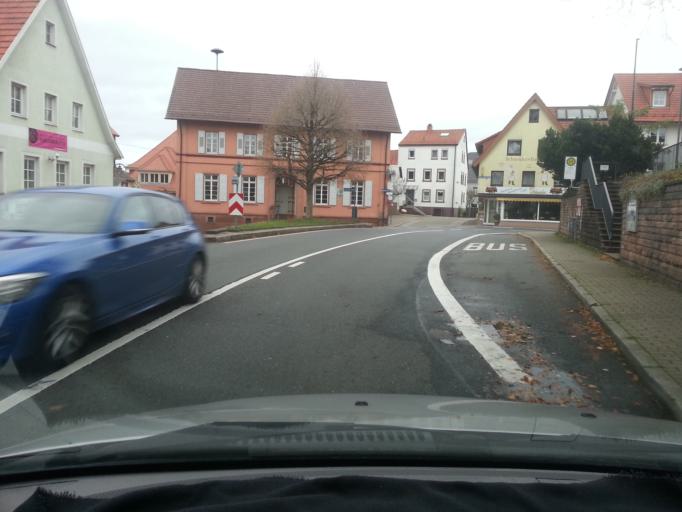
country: DE
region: Baden-Wuerttemberg
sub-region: Karlsruhe Region
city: Gaiberg
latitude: 49.3660
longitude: 8.7501
